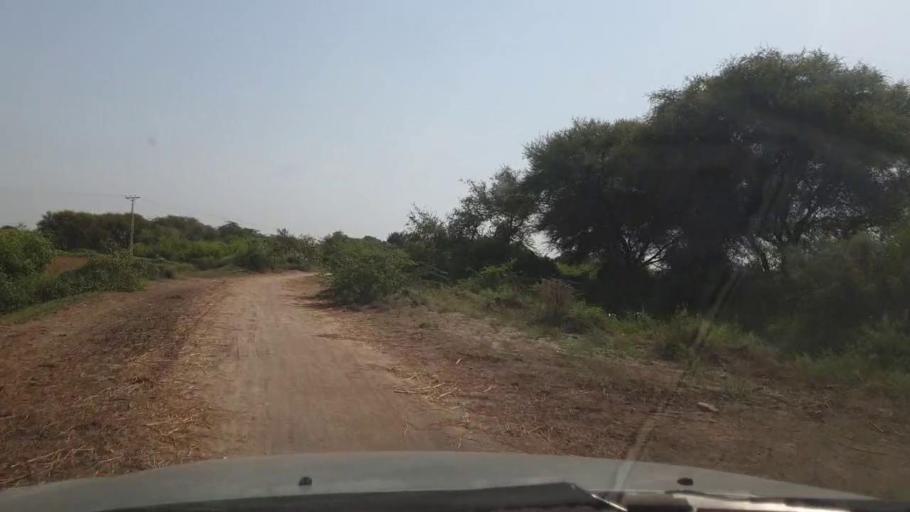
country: PK
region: Sindh
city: Bulri
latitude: 24.8706
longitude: 68.3105
